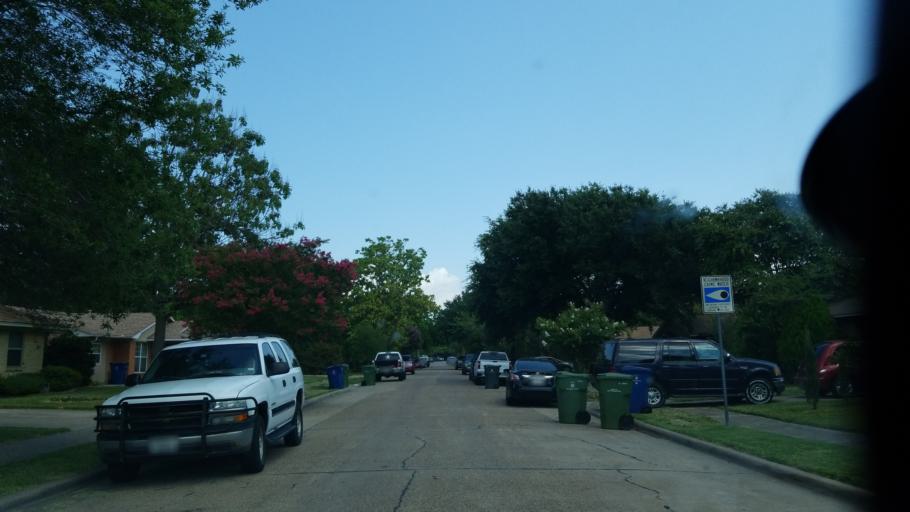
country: US
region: Texas
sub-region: Dallas County
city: Garland
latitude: 32.9270
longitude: -96.6480
